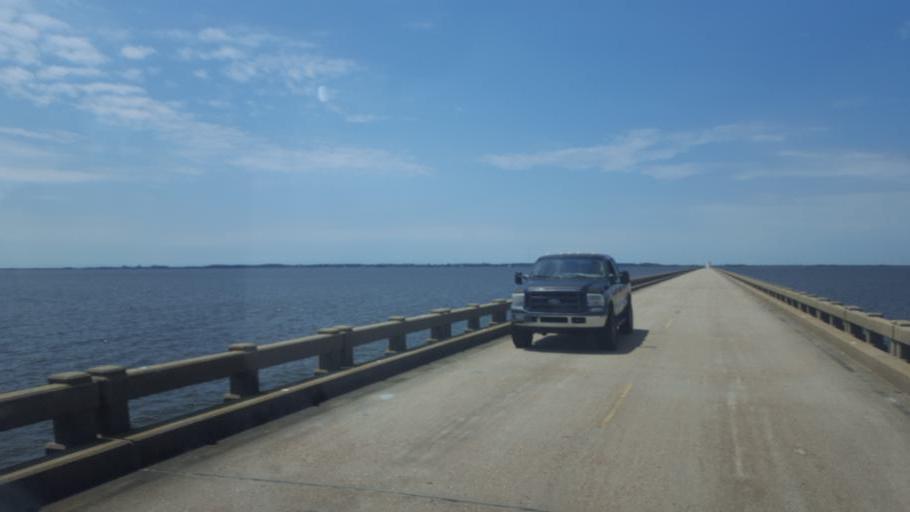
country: US
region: North Carolina
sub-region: Dare County
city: Manteo
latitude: 35.9257
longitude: -75.7283
